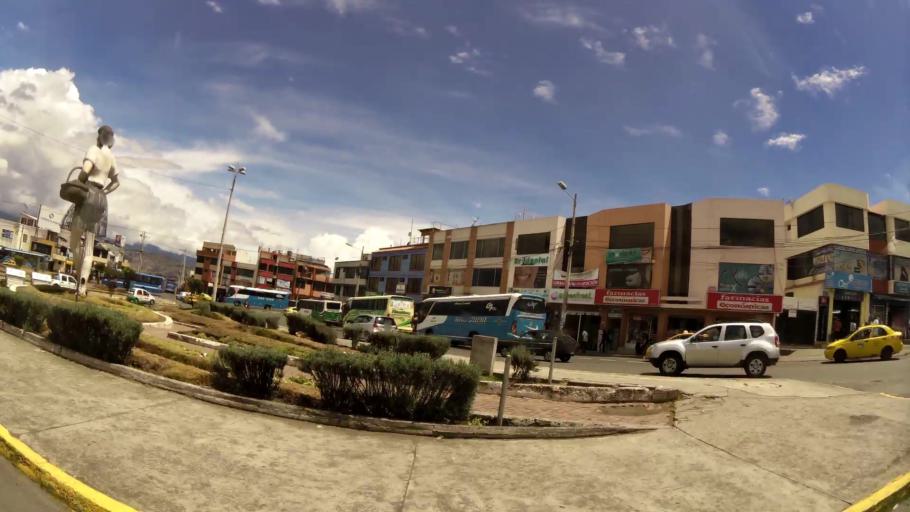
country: EC
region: Tungurahua
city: Ambato
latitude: -1.2754
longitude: -78.6304
